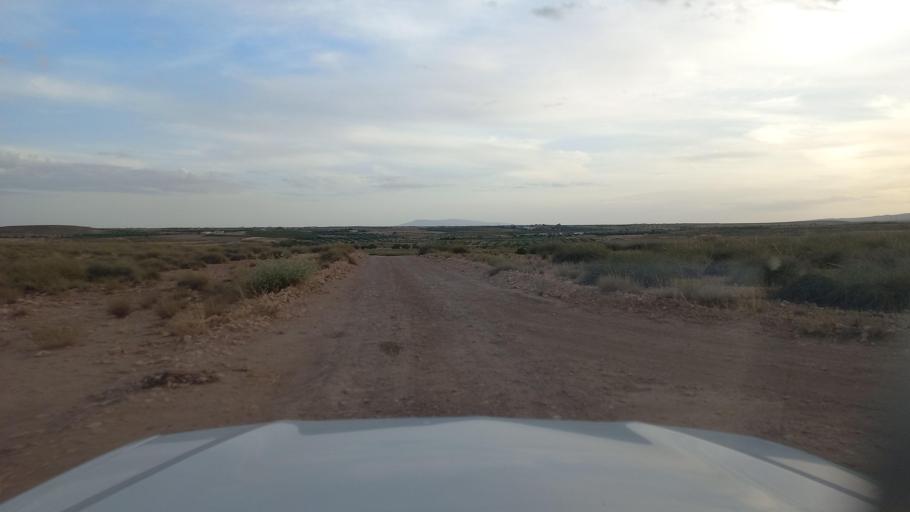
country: TN
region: Al Qasrayn
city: Sbiba
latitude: 35.4177
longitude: 9.0881
